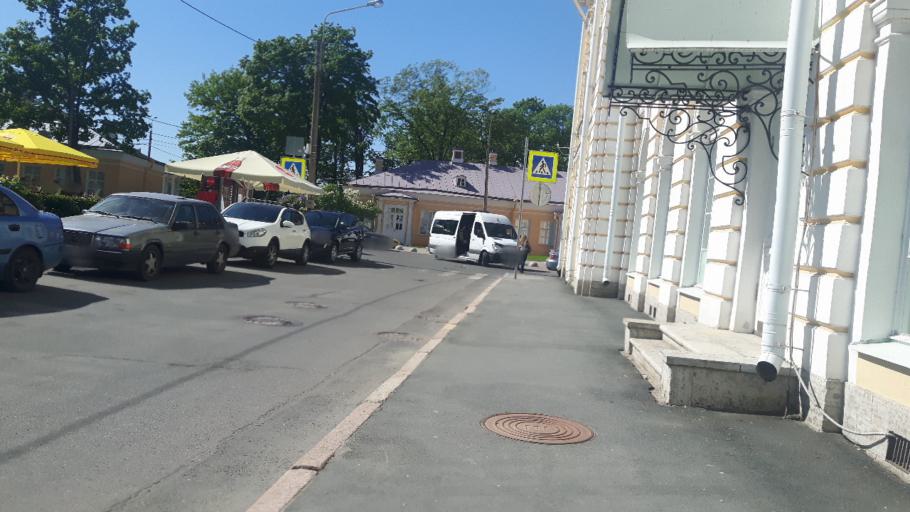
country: RU
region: St.-Petersburg
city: Peterhof
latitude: 59.8833
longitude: 29.9127
